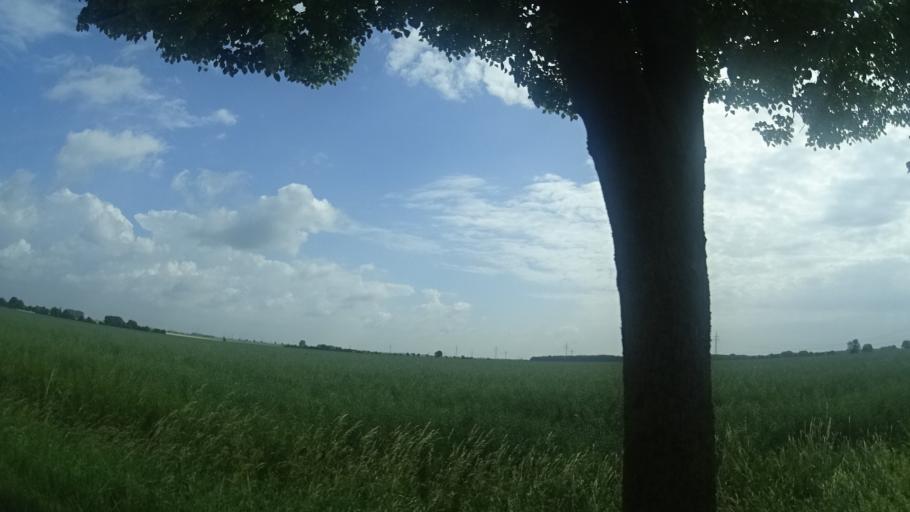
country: DE
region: Lower Saxony
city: Pattensen
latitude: 52.2275
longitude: 9.6806
